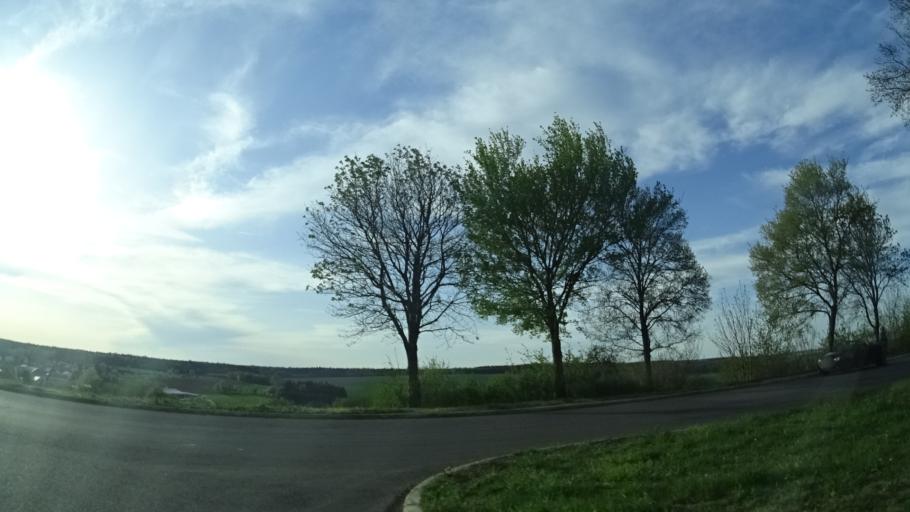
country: DE
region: Baden-Wuerttemberg
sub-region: Karlsruhe Region
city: Buchen
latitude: 49.5008
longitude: 9.2746
